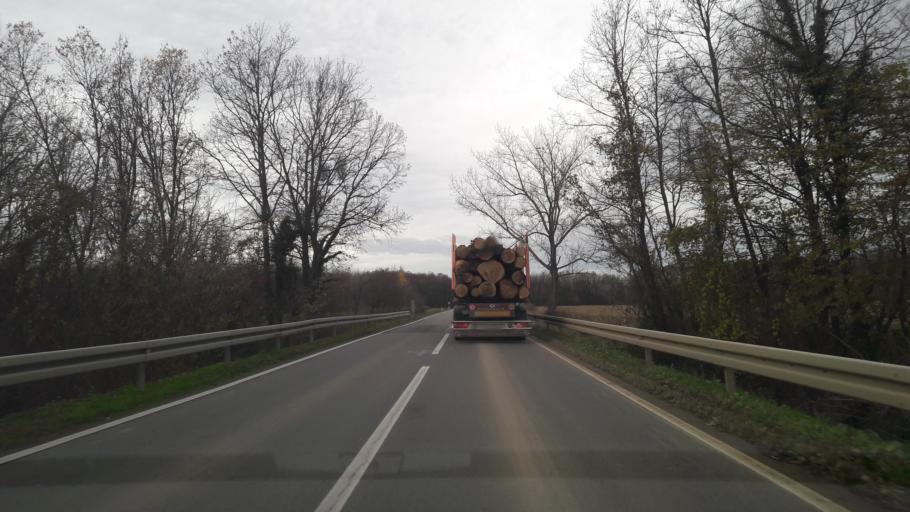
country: HR
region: Virovitick-Podravska
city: Orahovica
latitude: 45.5421
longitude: 17.9191
